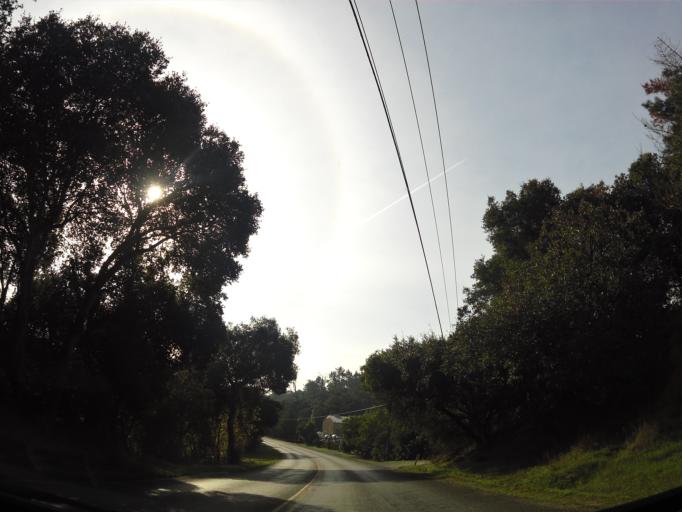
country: US
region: California
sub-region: Monterey County
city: Prunedale
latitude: 36.7975
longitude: -121.6165
